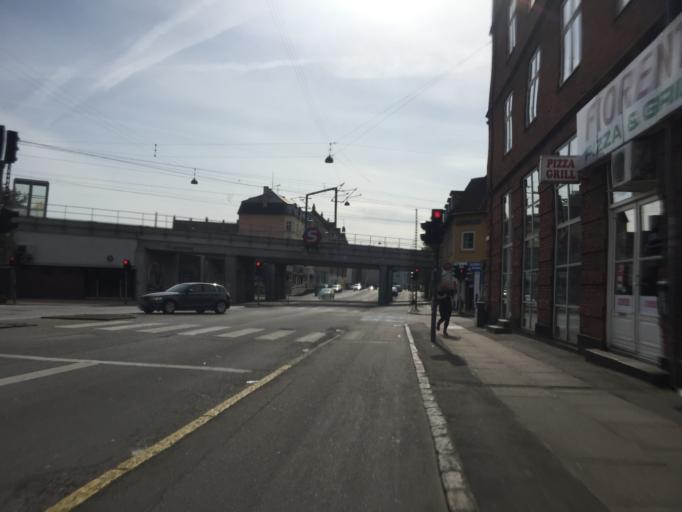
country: DK
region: Capital Region
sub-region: Kobenhavn
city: Vanlose
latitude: 55.6670
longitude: 12.5030
